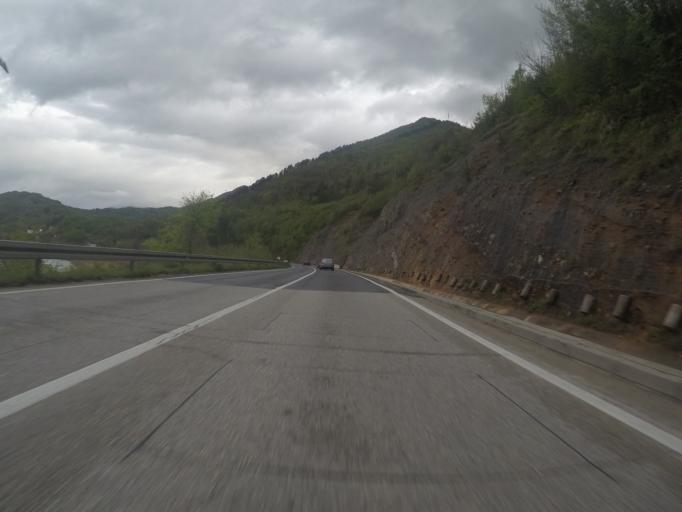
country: BA
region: Federation of Bosnia and Herzegovina
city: Konjic
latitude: 43.6800
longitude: 17.9049
